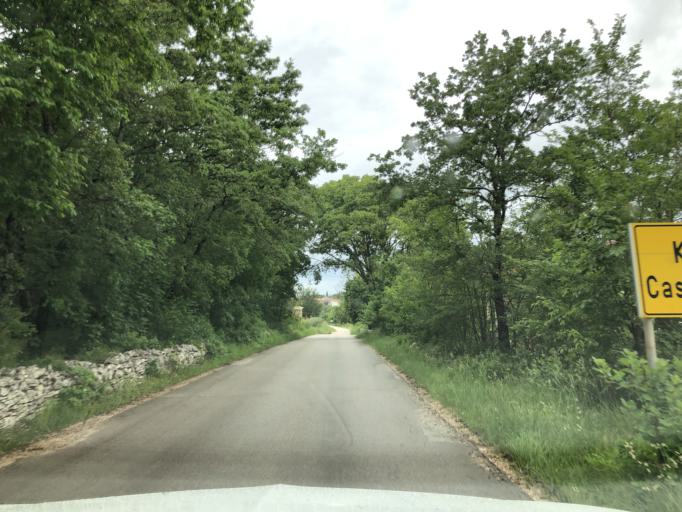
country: HR
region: Istarska
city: Buje
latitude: 45.4389
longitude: 13.6618
